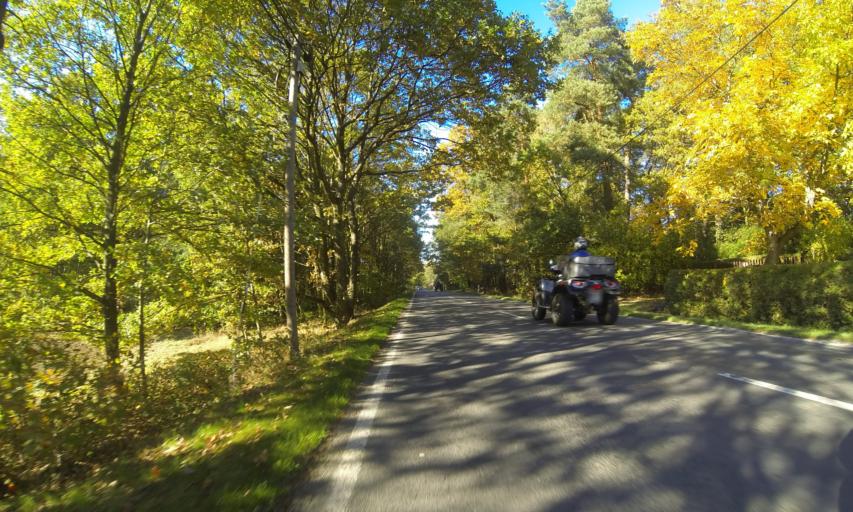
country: DE
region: Saxony
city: Weinbohla
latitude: 51.1937
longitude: 13.6041
